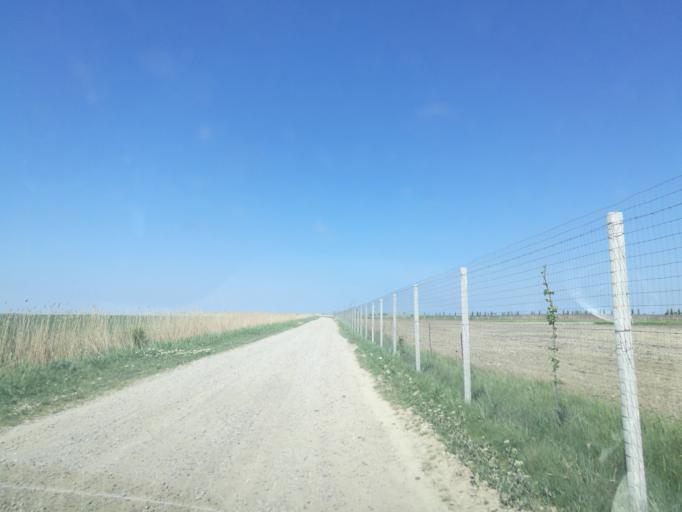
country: RO
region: Ialomita
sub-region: Comuna Adancata
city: Adancata
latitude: 44.7811
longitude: 26.4682
